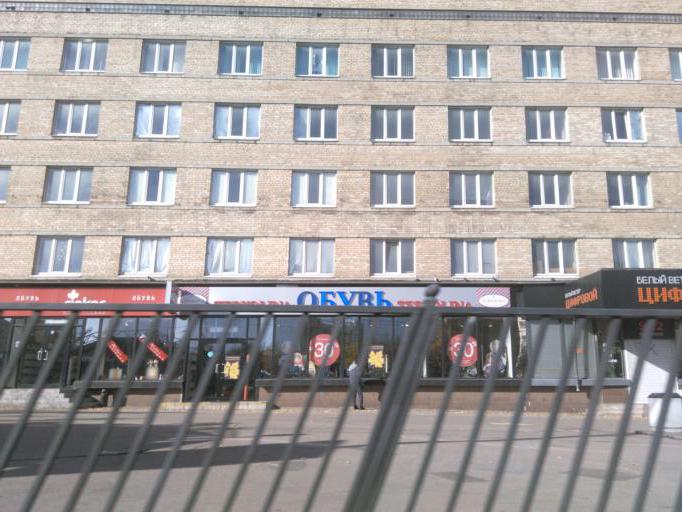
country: RU
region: Moskovskaya
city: Leninskiye Gory
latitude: 55.6885
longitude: 37.5741
